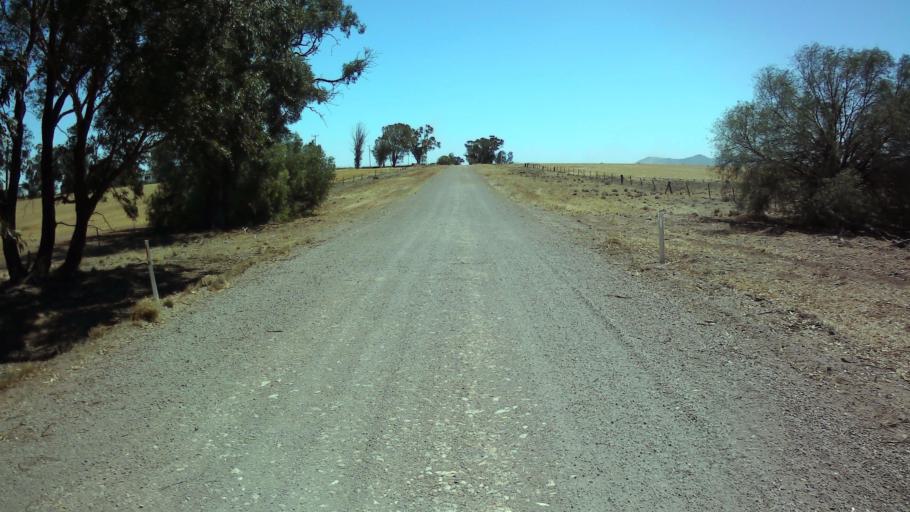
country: AU
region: New South Wales
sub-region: Forbes
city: Forbes
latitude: -33.6984
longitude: 147.7071
